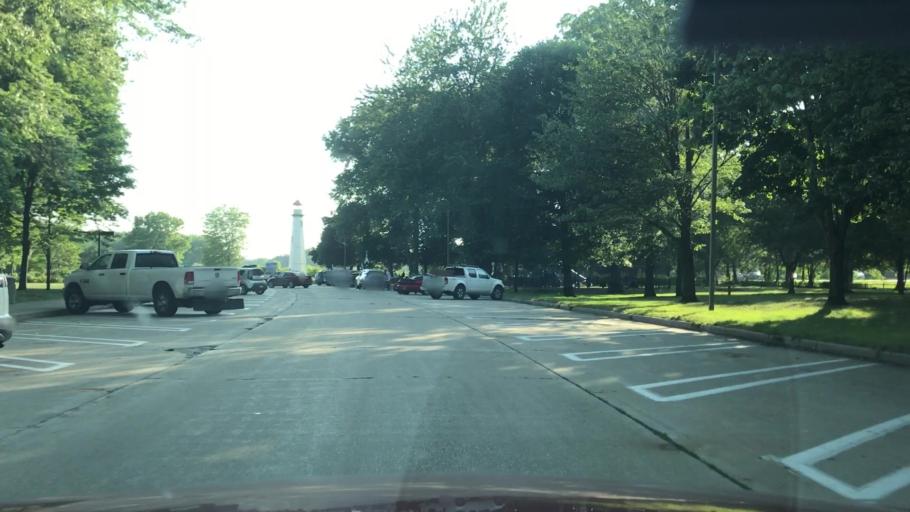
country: US
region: Michigan
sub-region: Berrien County
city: New Buffalo
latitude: 41.7658
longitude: -86.7397
